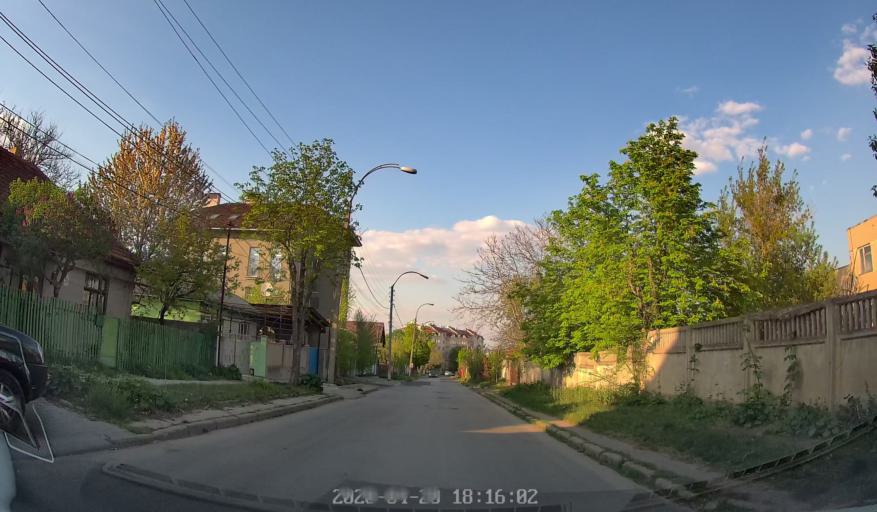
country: MD
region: Chisinau
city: Chisinau
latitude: 46.9993
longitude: 28.8328
